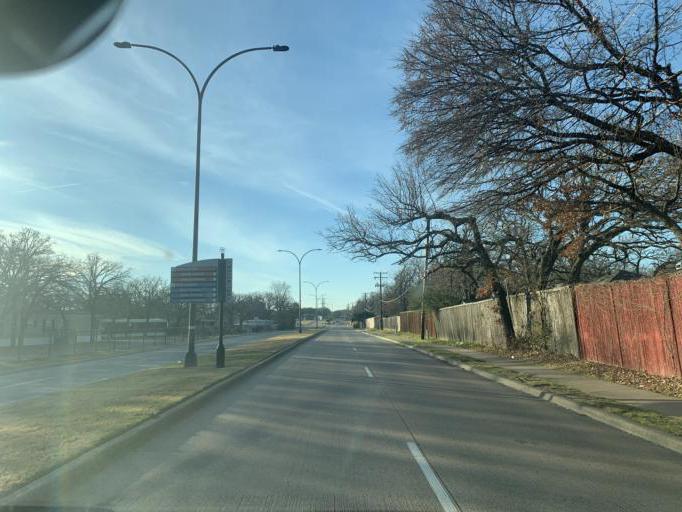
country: US
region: Texas
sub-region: Tarrant County
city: Arlington
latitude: 32.7694
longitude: -97.0738
